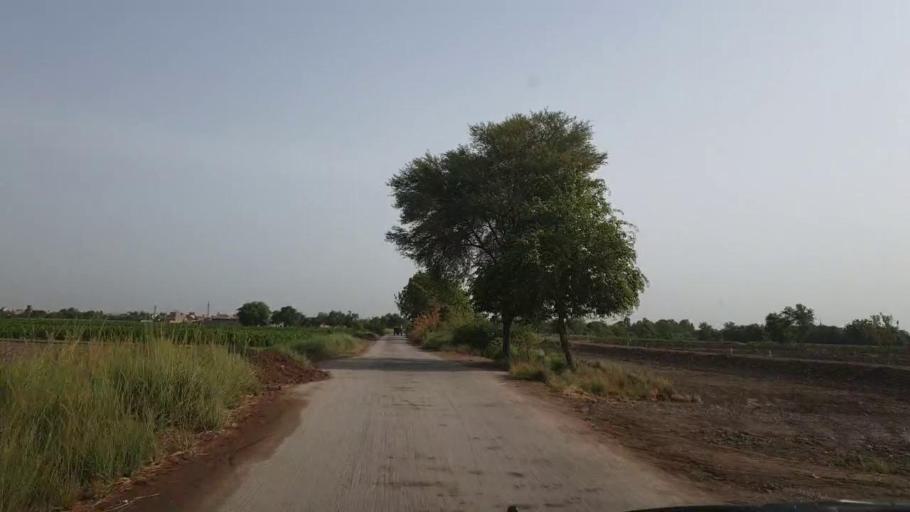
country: PK
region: Sindh
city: Nawabshah
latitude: 26.2270
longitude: 68.4054
